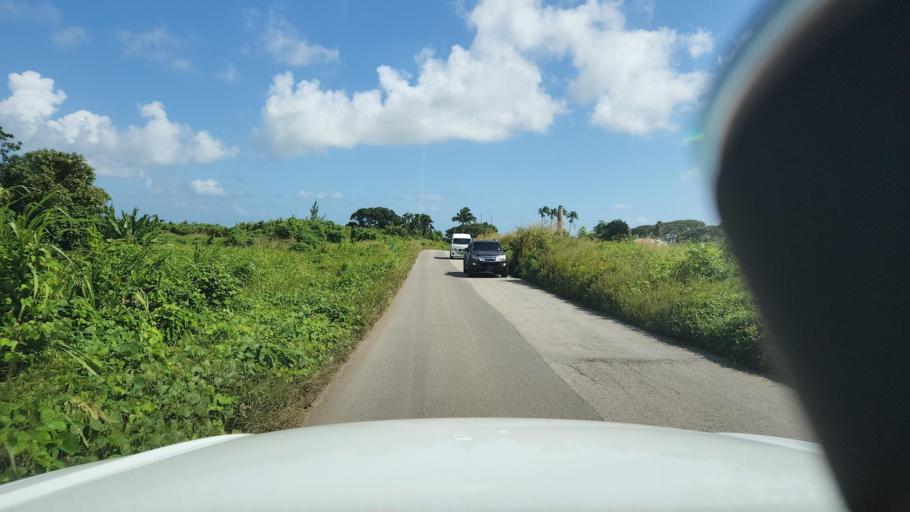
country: BB
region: Saint John
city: Four Cross Roads
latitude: 13.1701
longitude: -59.4881
